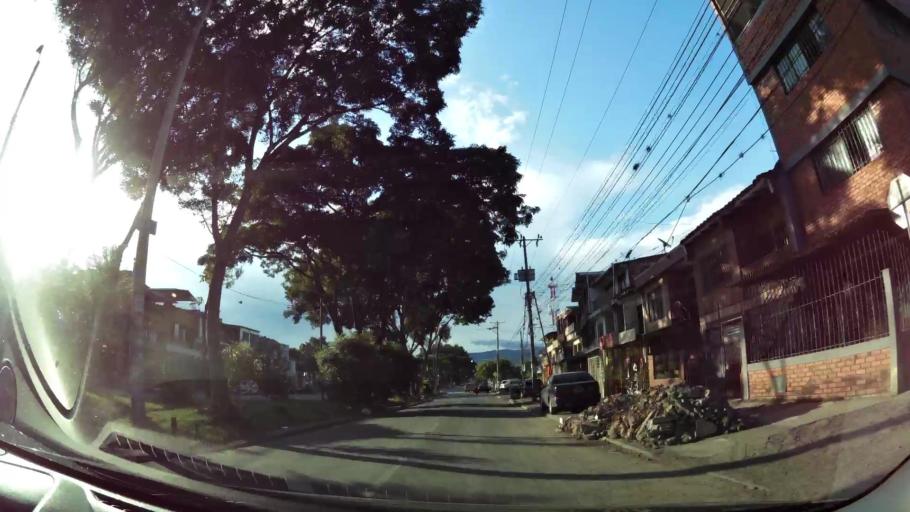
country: CO
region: Valle del Cauca
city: Cali
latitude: 3.4075
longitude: -76.5033
